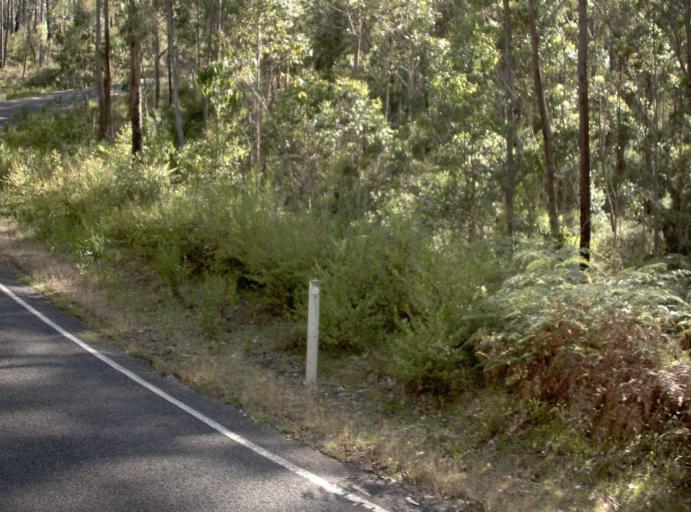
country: AU
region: Victoria
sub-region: East Gippsland
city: Lakes Entrance
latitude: -37.6615
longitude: 148.4766
